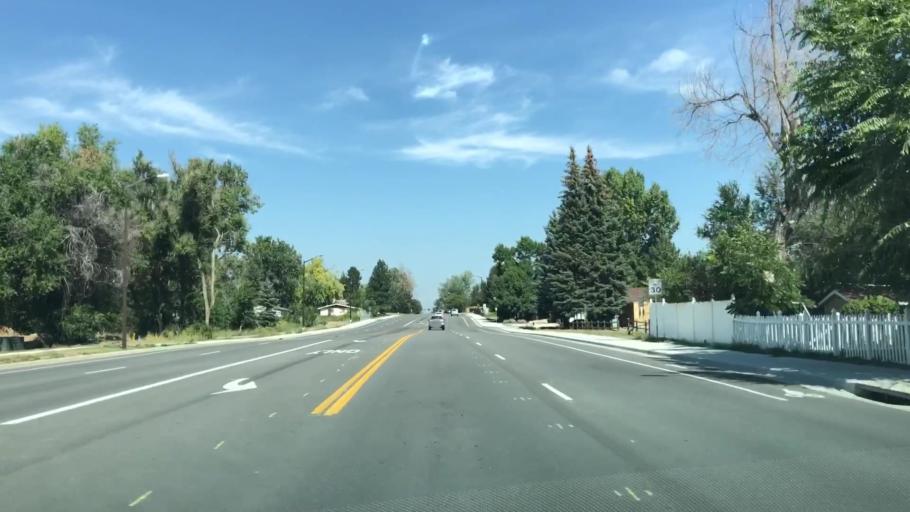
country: US
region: Colorado
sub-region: Larimer County
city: Loveland
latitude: 40.4016
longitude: -105.0970
